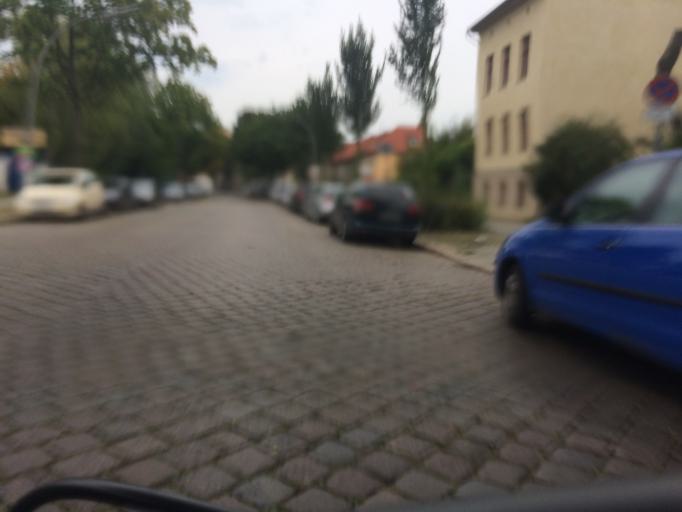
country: DE
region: Berlin
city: Gesundbrunnen
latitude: 52.5641
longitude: 13.3836
